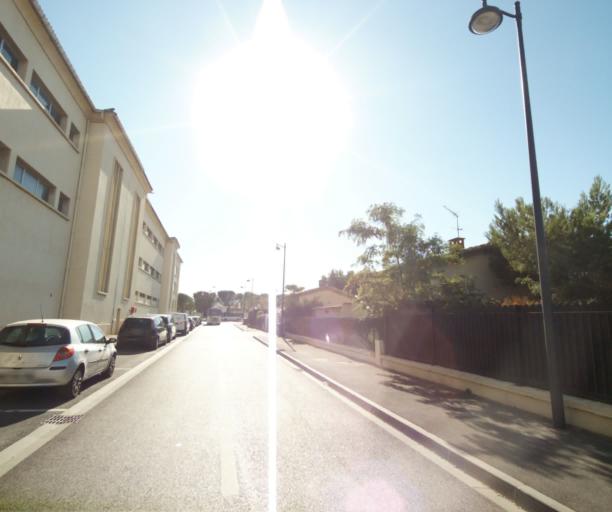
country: FR
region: Provence-Alpes-Cote d'Azur
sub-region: Departement des Bouches-du-Rhone
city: Saint-Victoret
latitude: 43.4163
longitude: 5.2446
